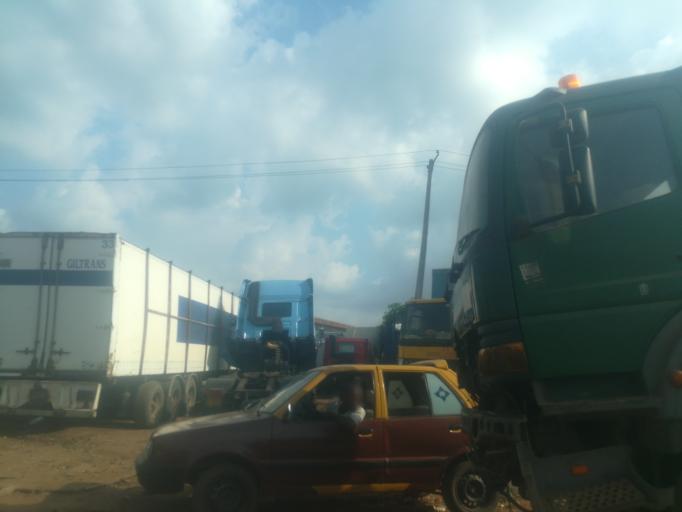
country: NG
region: Oyo
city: Moniya
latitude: 7.4892
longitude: 3.9152
